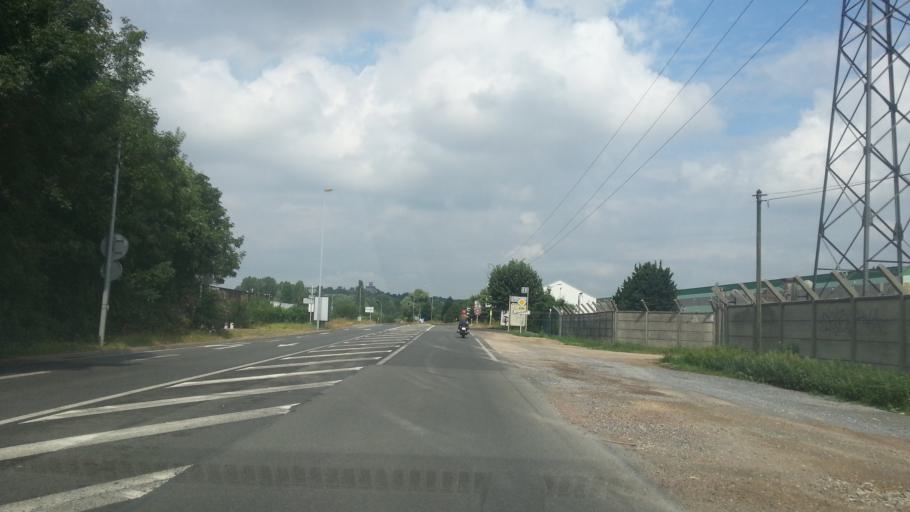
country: FR
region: Picardie
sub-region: Departement de l'Oise
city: Thiverny
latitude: 49.2448
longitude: 2.4409
